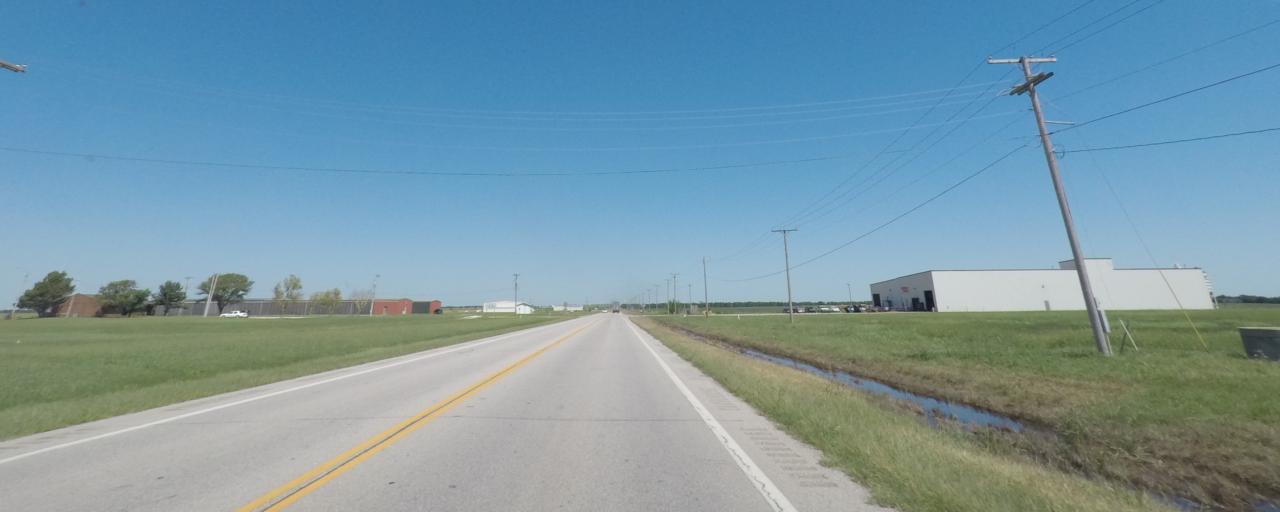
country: US
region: Kansas
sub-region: Sumner County
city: Wellington
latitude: 37.3238
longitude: -97.3848
